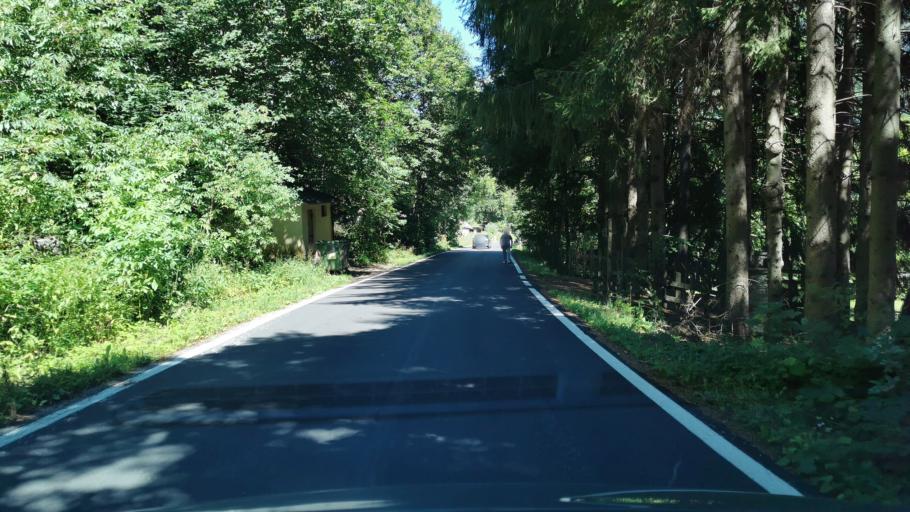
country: IT
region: Piedmont
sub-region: Provincia di Cuneo
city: Demonte
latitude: 44.2240
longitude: 7.2944
